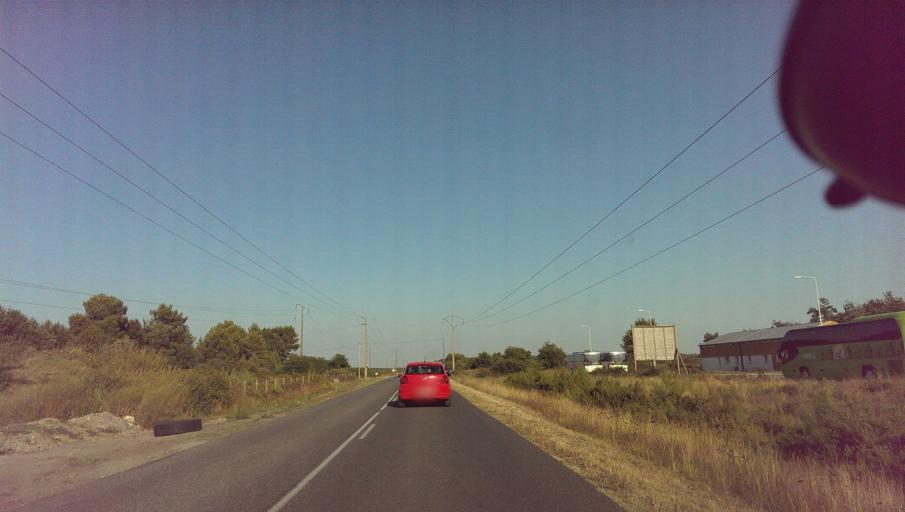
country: FR
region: Aquitaine
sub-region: Departement des Landes
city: Mimizan
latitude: 44.1878
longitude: -1.2082
